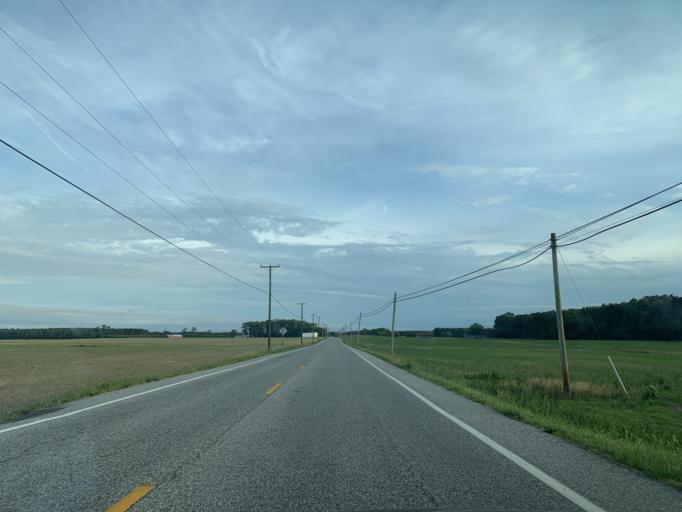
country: US
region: Maryland
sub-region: Worcester County
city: Snow Hill
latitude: 38.1637
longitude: -75.4013
